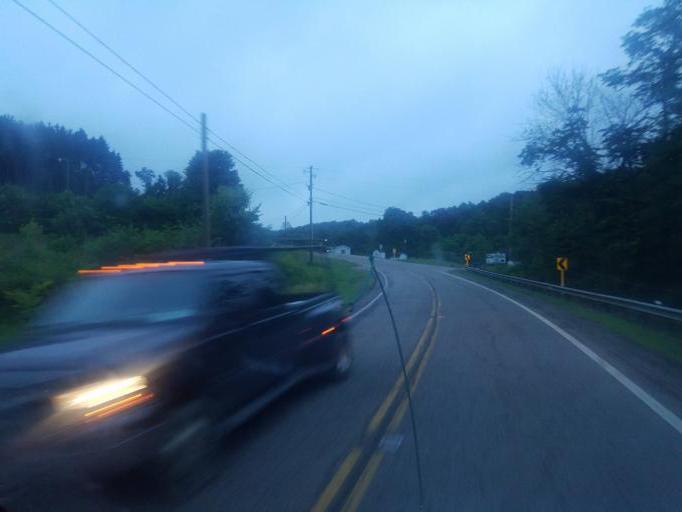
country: US
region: Ohio
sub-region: Carroll County
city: Carrollton
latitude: 40.5816
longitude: -81.0303
